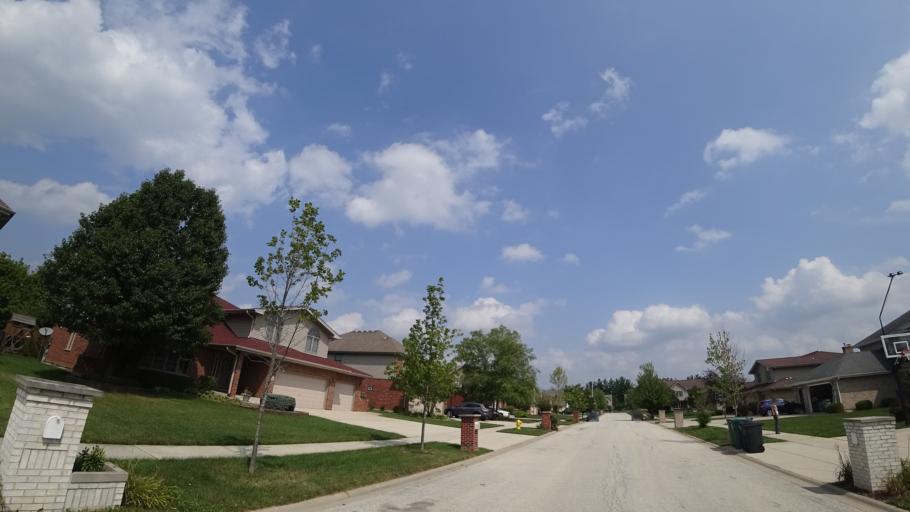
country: US
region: Illinois
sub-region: Will County
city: Goodings Grove
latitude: 41.6362
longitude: -87.9057
